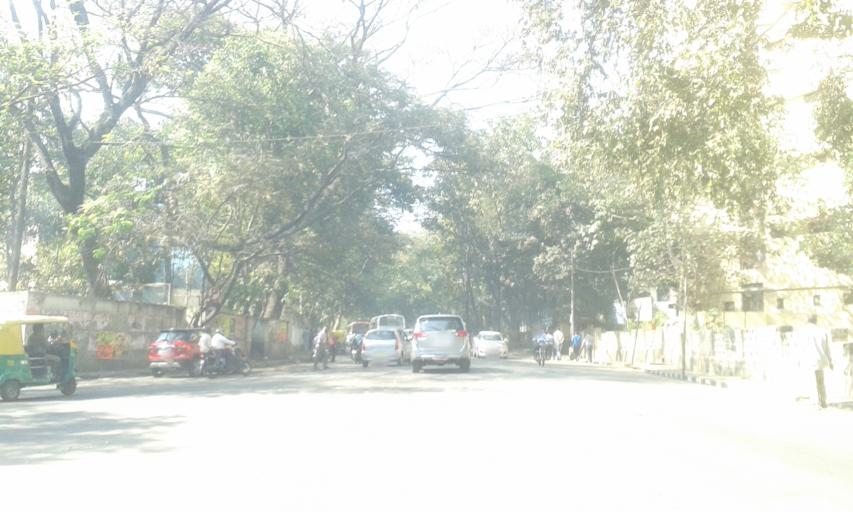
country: IN
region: Karnataka
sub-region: Bangalore Urban
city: Bangalore
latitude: 13.0092
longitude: 77.5712
